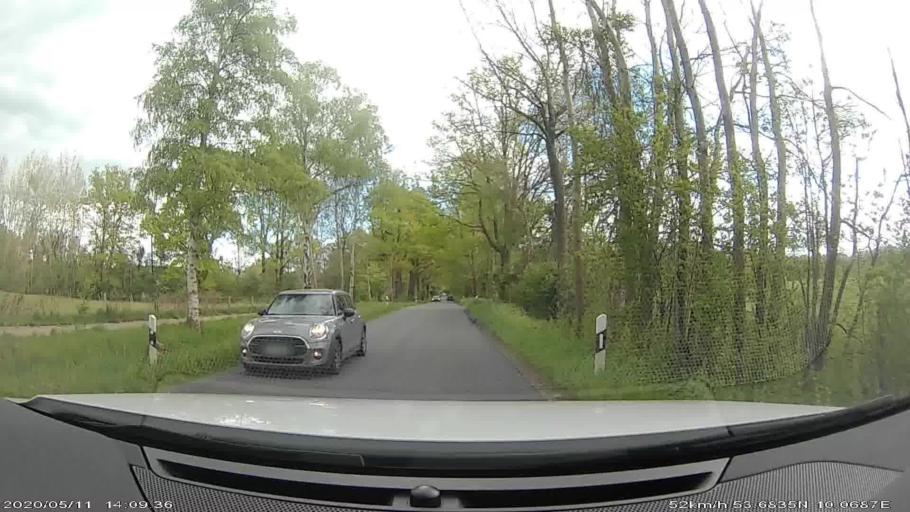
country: DE
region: Hamburg
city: Lemsahl-Mellingstedt
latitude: 53.6825
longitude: 10.0882
